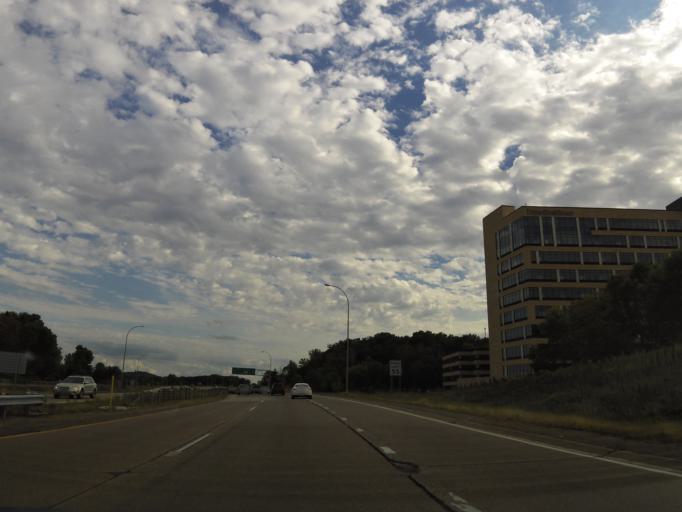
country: US
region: Minnesota
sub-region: Hennepin County
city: Edina
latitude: 44.8961
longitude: -93.4012
